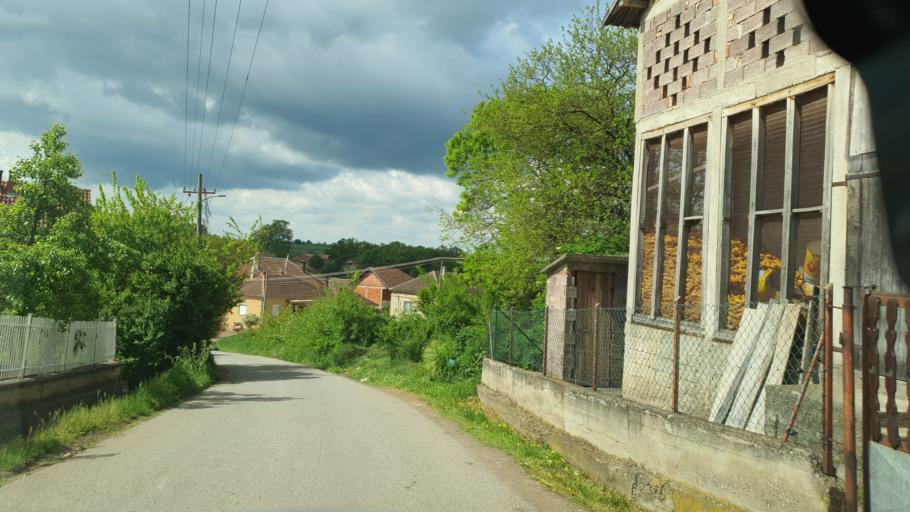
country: RS
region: Central Serbia
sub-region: Pomoravski Okrug
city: Paracin
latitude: 43.9376
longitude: 21.4932
